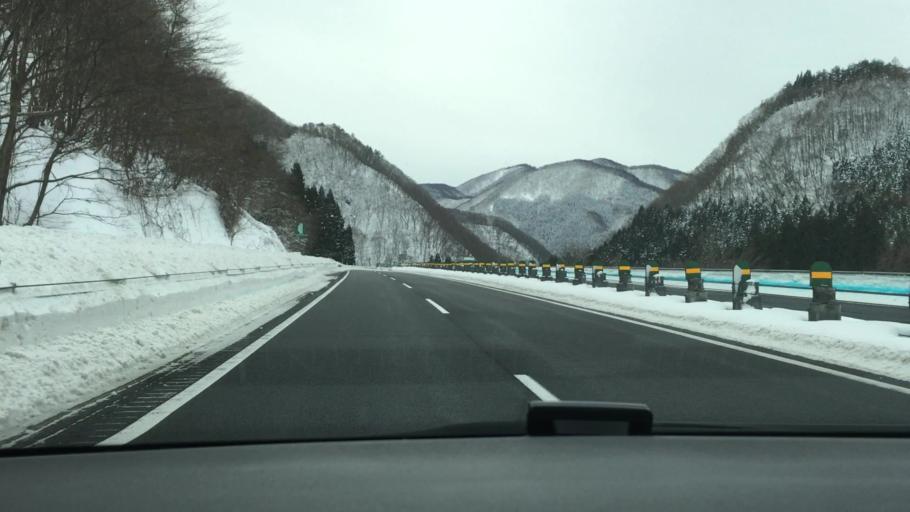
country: JP
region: Akita
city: Hanawa
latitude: 40.1238
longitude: 140.9077
